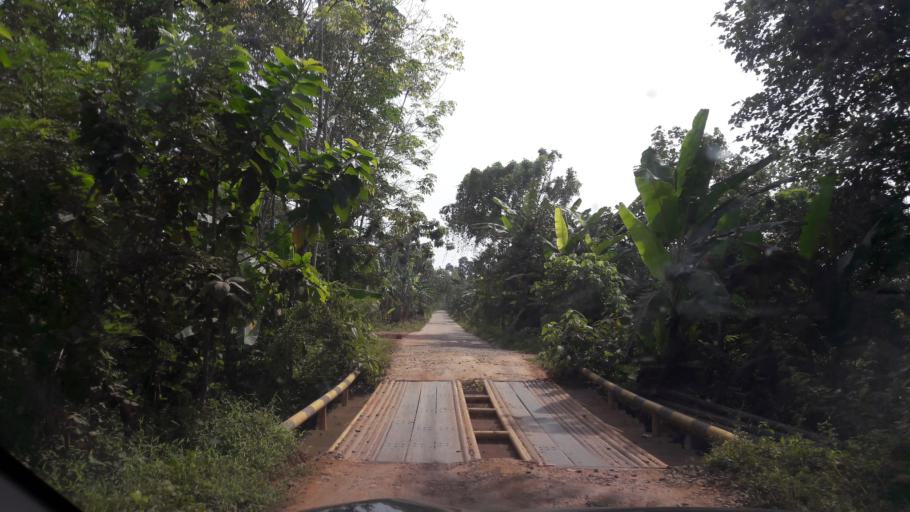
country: ID
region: South Sumatra
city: Prabumulih
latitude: -3.3256
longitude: 104.1133
